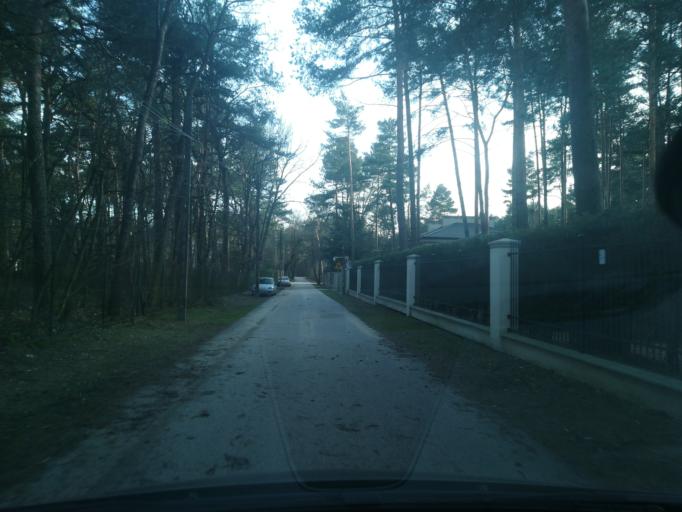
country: PL
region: Masovian Voivodeship
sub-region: Powiat piaseczynski
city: Konstancin-Jeziorna
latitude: 52.0727
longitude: 21.0948
